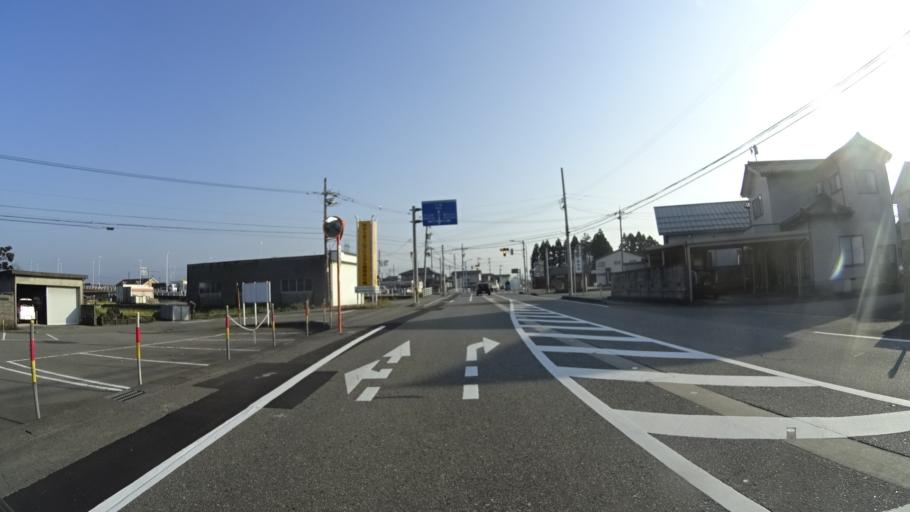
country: JP
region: Toyama
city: Toyama-shi
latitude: 36.6854
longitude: 137.2716
